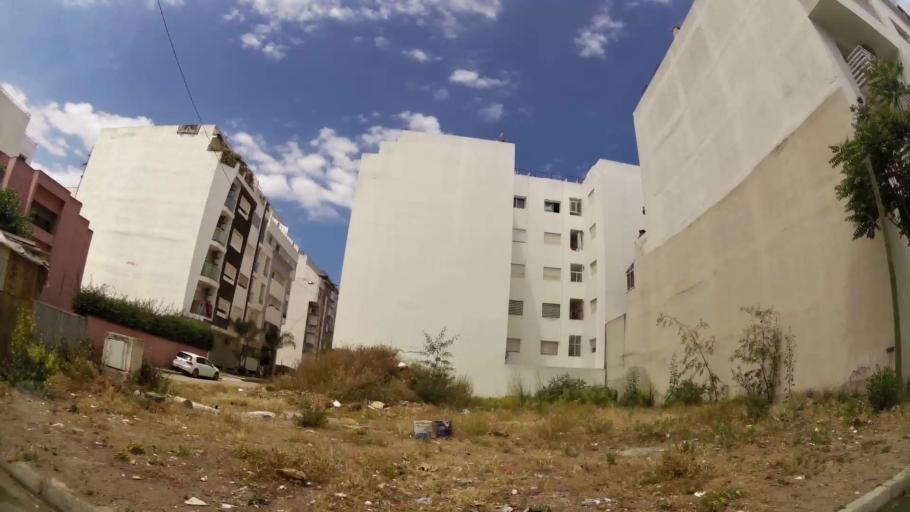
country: MA
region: Gharb-Chrarda-Beni Hssen
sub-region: Kenitra Province
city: Kenitra
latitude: 34.2618
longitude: -6.5955
